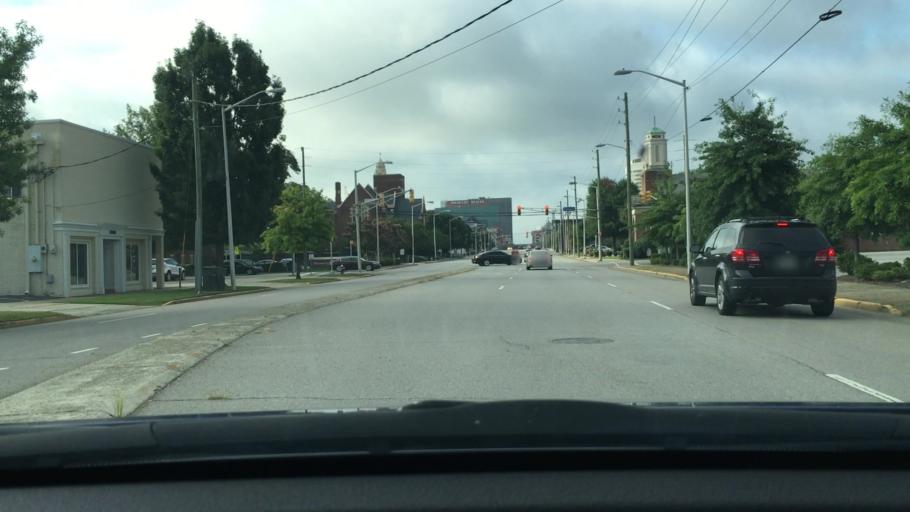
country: US
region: South Carolina
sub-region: Richland County
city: Columbia
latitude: 34.0132
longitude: -81.0371
